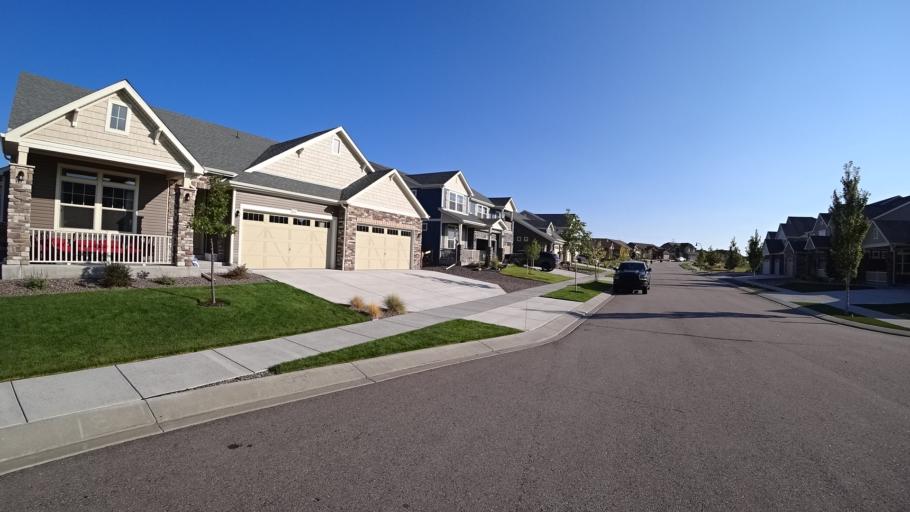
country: US
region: Colorado
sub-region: El Paso County
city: Cimarron Hills
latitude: 38.9343
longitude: -104.6700
